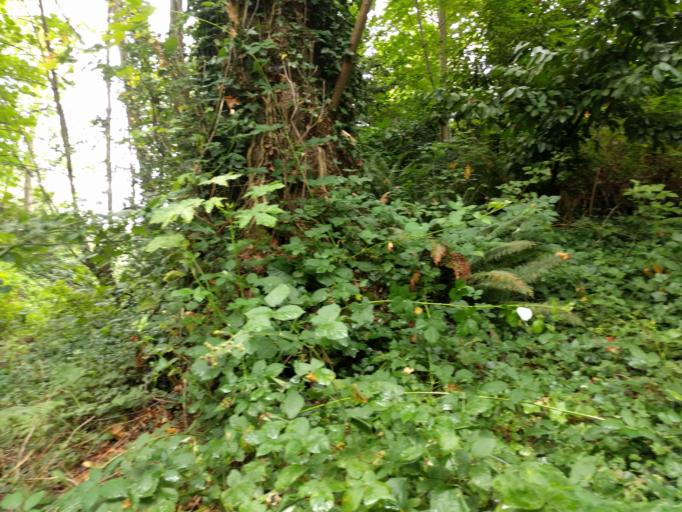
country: US
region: Washington
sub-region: King County
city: Des Moines
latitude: 47.3956
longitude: -122.3035
